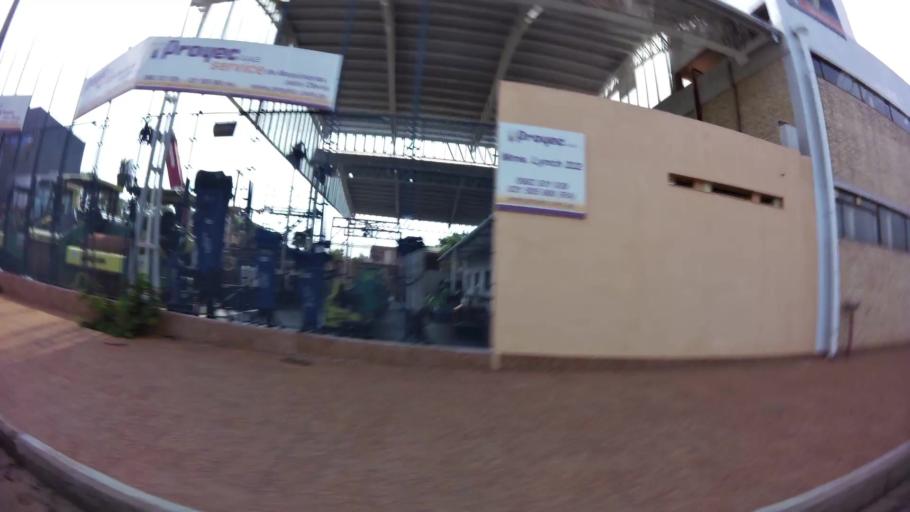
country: PY
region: Central
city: Fernando de la Mora
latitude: -25.3055
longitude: -57.5526
